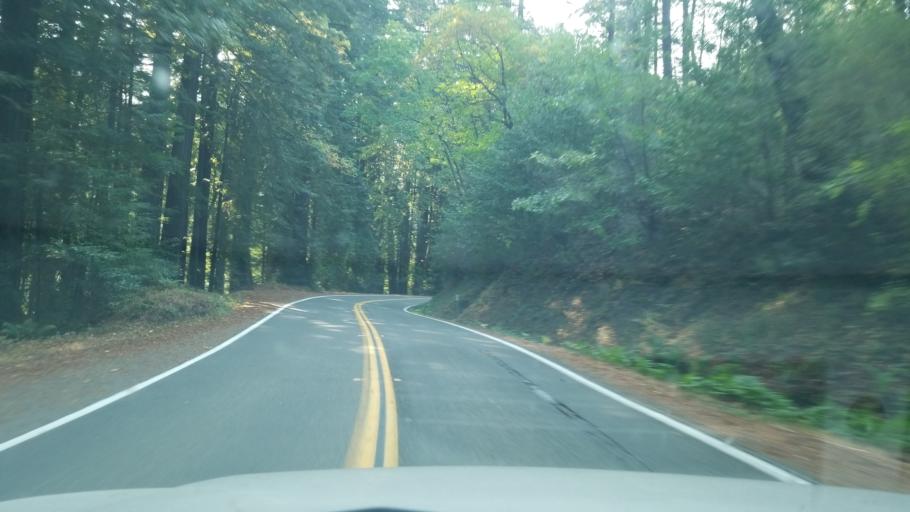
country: US
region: California
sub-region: Humboldt County
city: Redway
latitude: 40.2577
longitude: -123.8332
